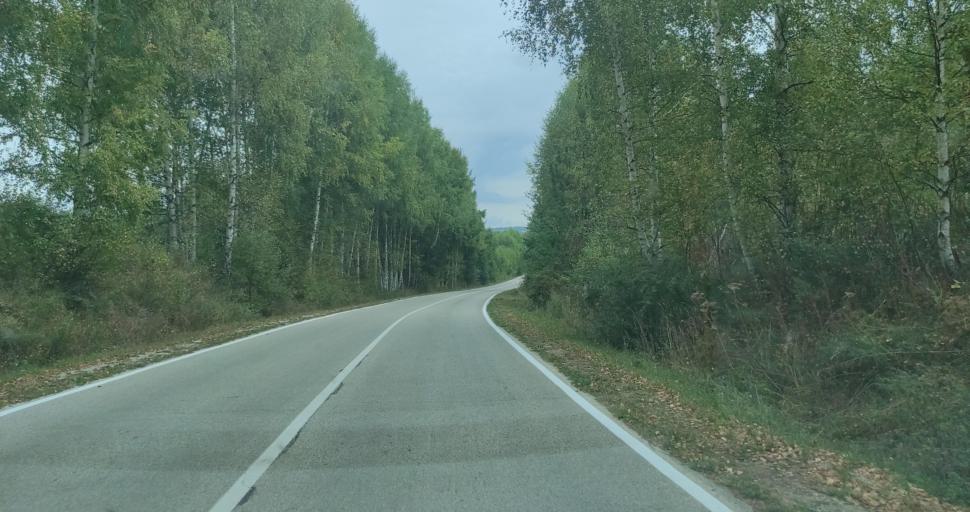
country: RS
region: Central Serbia
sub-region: Jablanicki Okrug
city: Crna Trava
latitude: 42.7171
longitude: 22.3302
